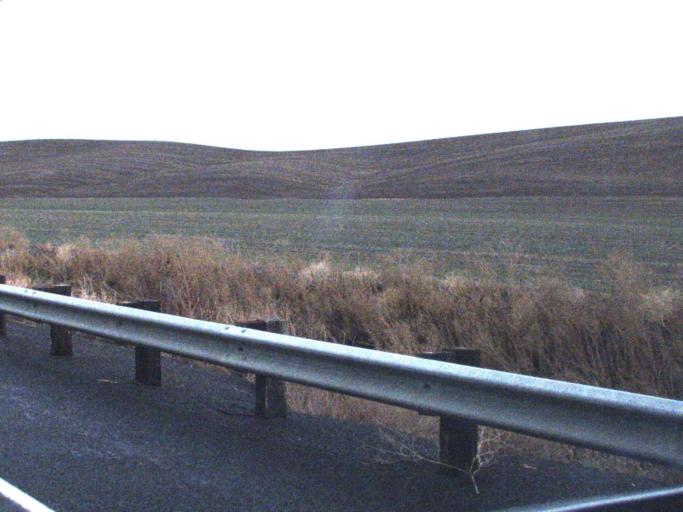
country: US
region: Washington
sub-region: Walla Walla County
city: Waitsburg
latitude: 46.2101
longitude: -118.1376
